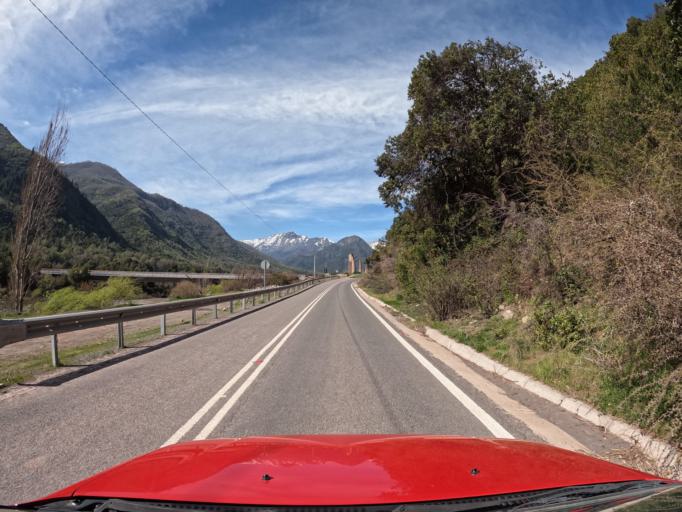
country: CL
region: O'Higgins
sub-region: Provincia de Colchagua
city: Chimbarongo
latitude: -35.0004
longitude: -70.7947
